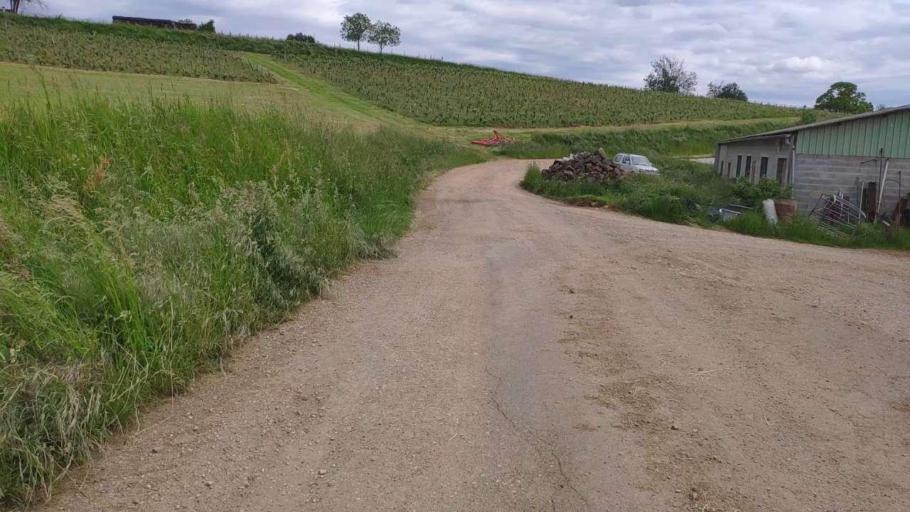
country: FR
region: Franche-Comte
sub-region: Departement du Jura
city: Bletterans
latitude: 46.7938
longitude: 5.5594
